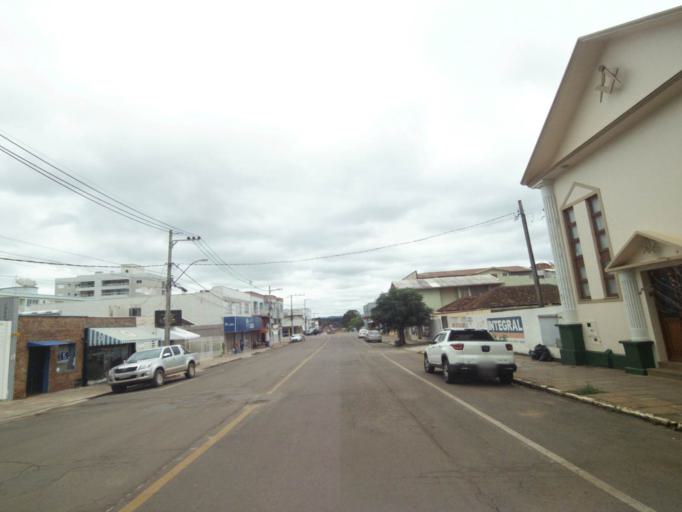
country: BR
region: Rio Grande do Sul
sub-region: Lagoa Vermelha
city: Lagoa Vermelha
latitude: -28.2112
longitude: -51.5222
